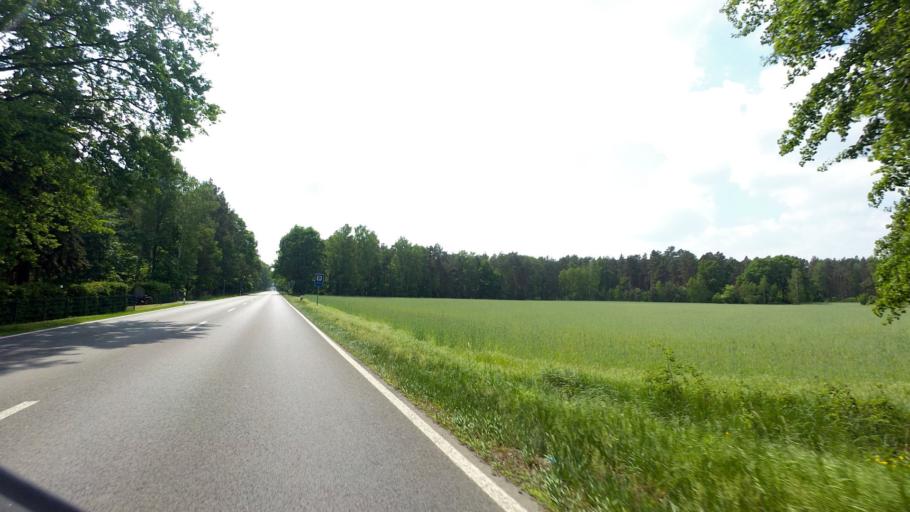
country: DE
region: Brandenburg
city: Cottbus
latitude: 51.7006
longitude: 14.3618
